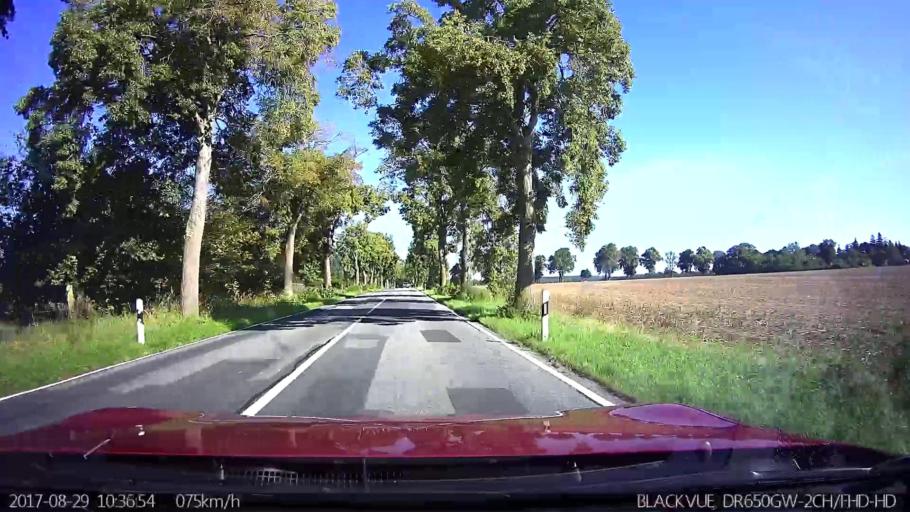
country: DE
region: Mecklenburg-Vorpommern
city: Tribsees
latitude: 54.1511
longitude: 12.8036
